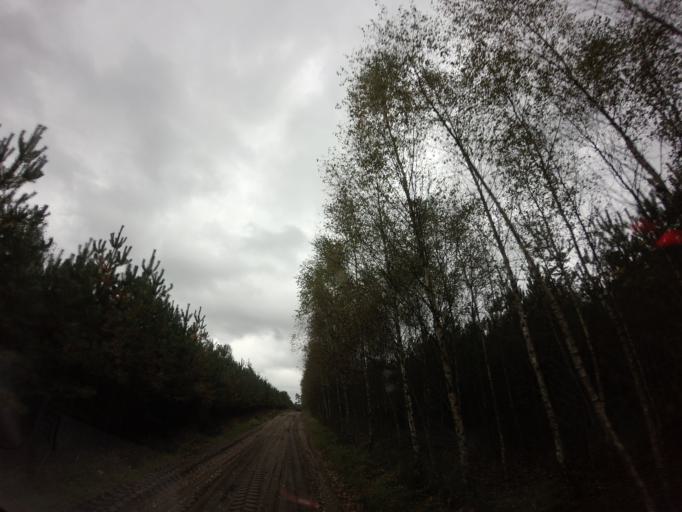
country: PL
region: West Pomeranian Voivodeship
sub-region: Powiat choszczenski
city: Drawno
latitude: 53.2364
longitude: 15.7874
